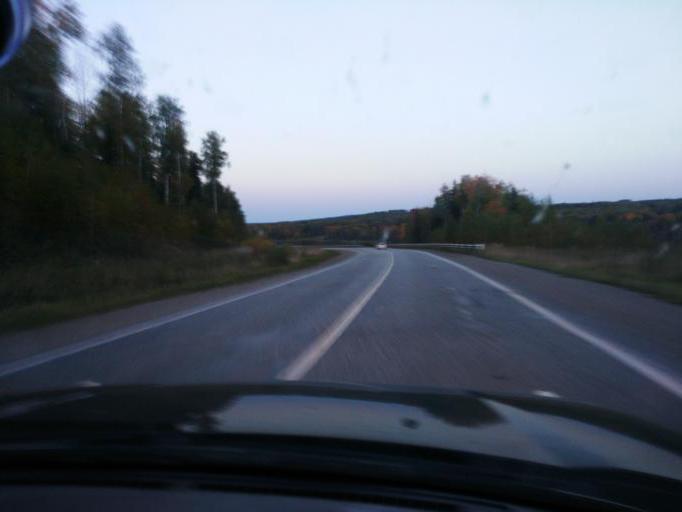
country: RU
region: Perm
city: Verkhnechusovskiye Gorodki
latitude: 58.2941
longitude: 56.8742
